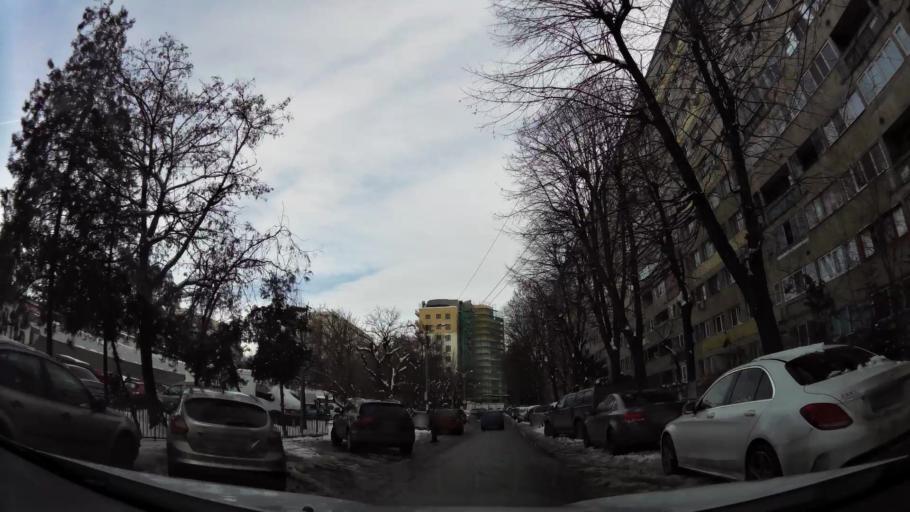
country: RO
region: Ilfov
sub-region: Comuna Popesti-Leordeni
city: Popesti-Leordeni
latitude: 44.3819
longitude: 26.1174
